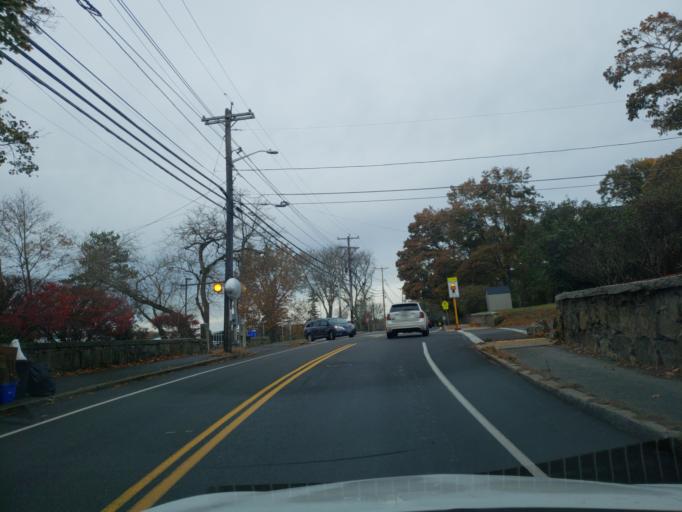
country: US
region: Massachusetts
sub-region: Essex County
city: Andover
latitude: 42.6596
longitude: -71.1511
